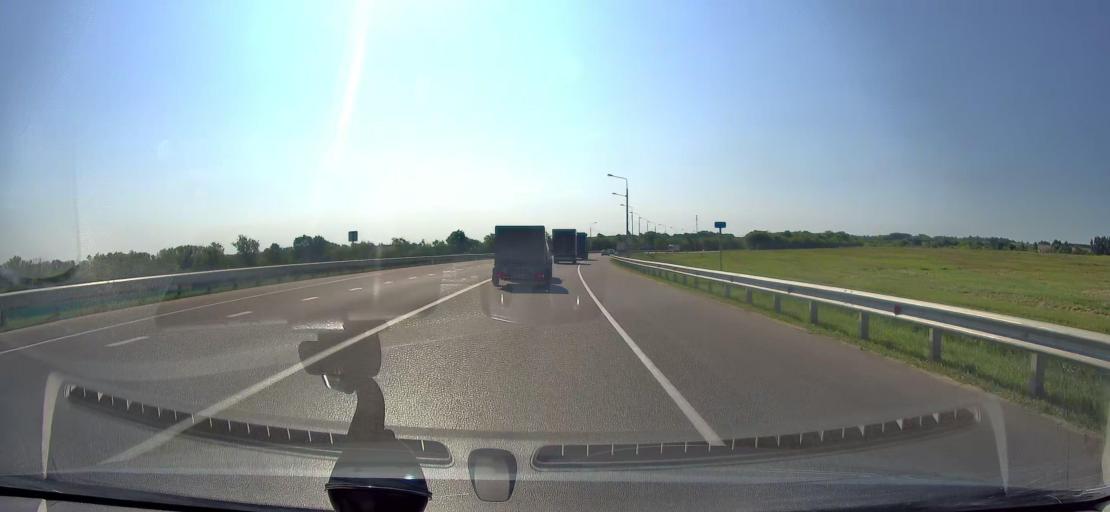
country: RU
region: Orjol
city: Kromy
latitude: 52.6480
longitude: 35.7413
